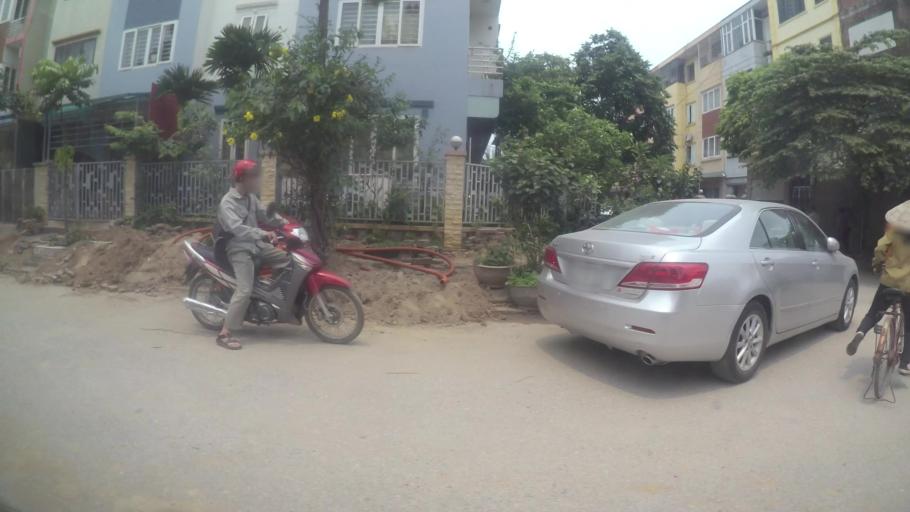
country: VN
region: Ha Noi
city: Ha Dong
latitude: 20.9759
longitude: 105.7653
